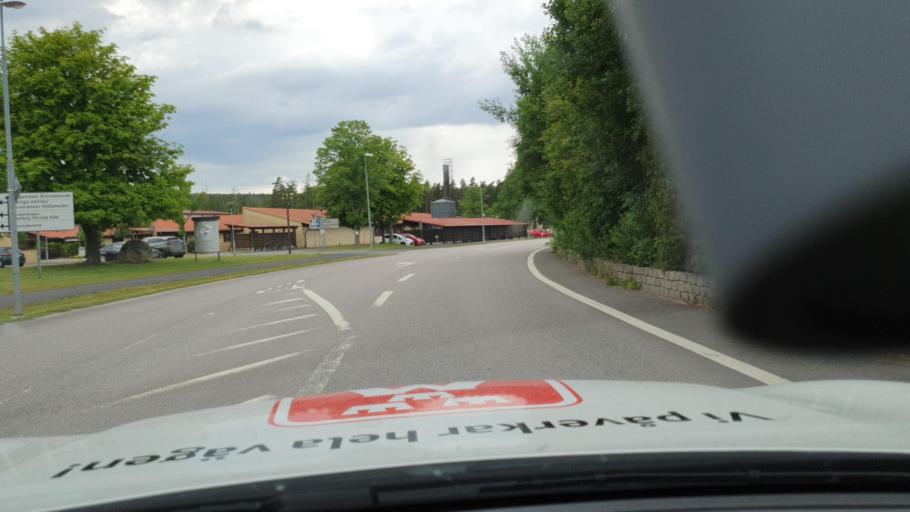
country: SE
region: Vaestra Goetaland
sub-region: Karlsborgs Kommun
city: Karlsborg
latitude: 58.5416
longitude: 14.4812
